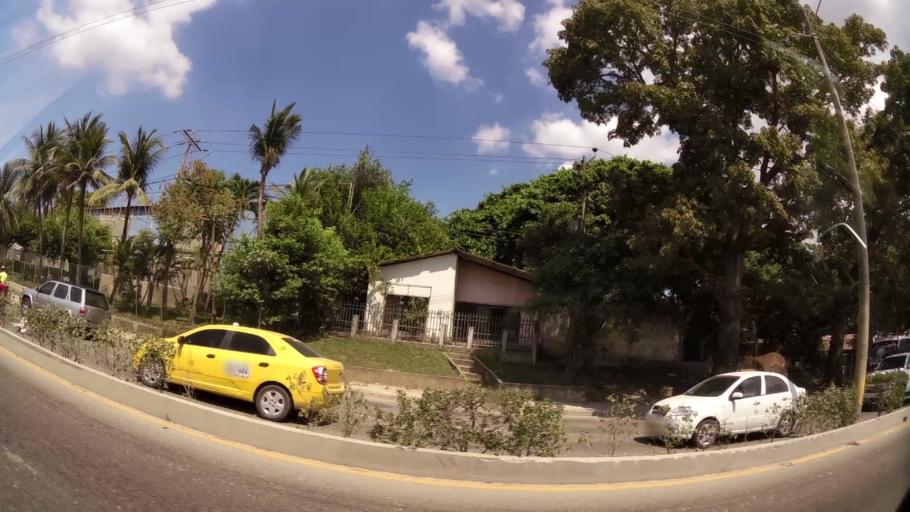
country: CO
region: Bolivar
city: Cartagena
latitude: 10.3546
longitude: -75.5020
